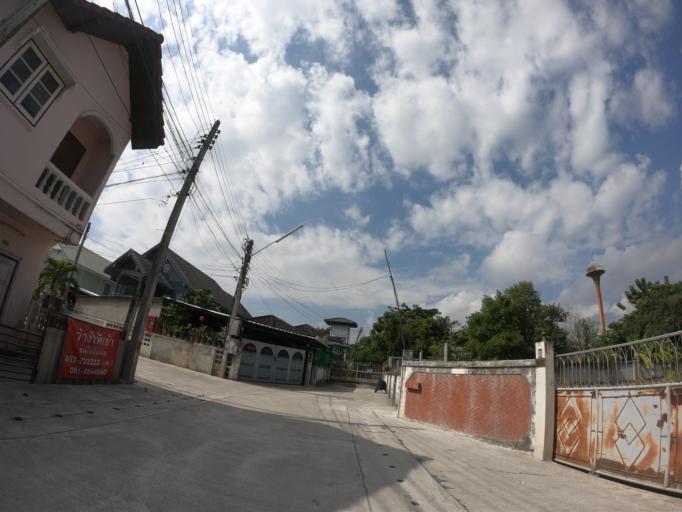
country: TH
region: Chiang Mai
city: Chiang Mai
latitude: 18.7710
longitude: 98.9818
